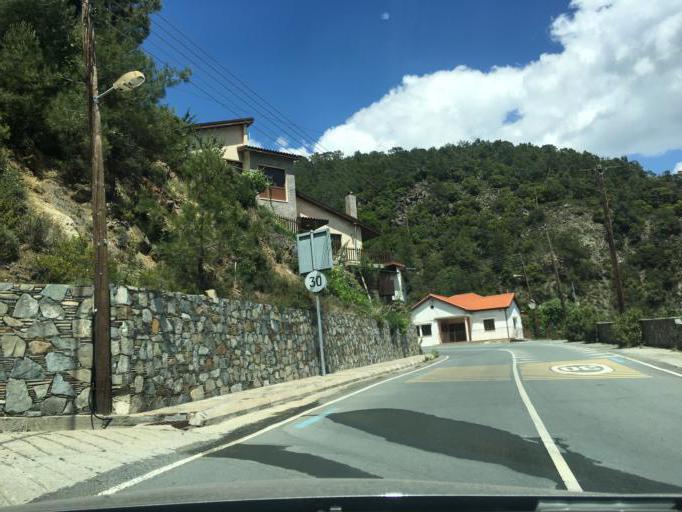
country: CY
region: Limassol
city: Pelendri
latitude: 34.9205
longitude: 32.9351
